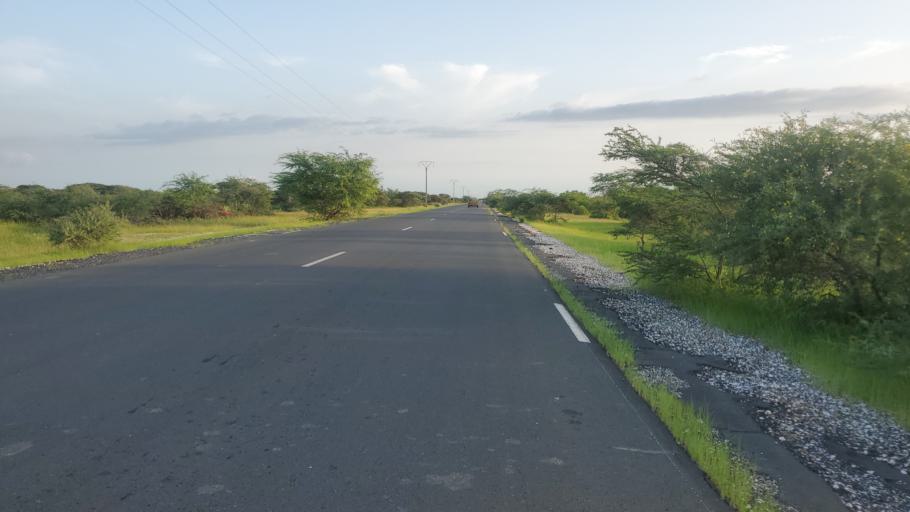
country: SN
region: Saint-Louis
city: Saint-Louis
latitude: 16.1786
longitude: -16.4096
